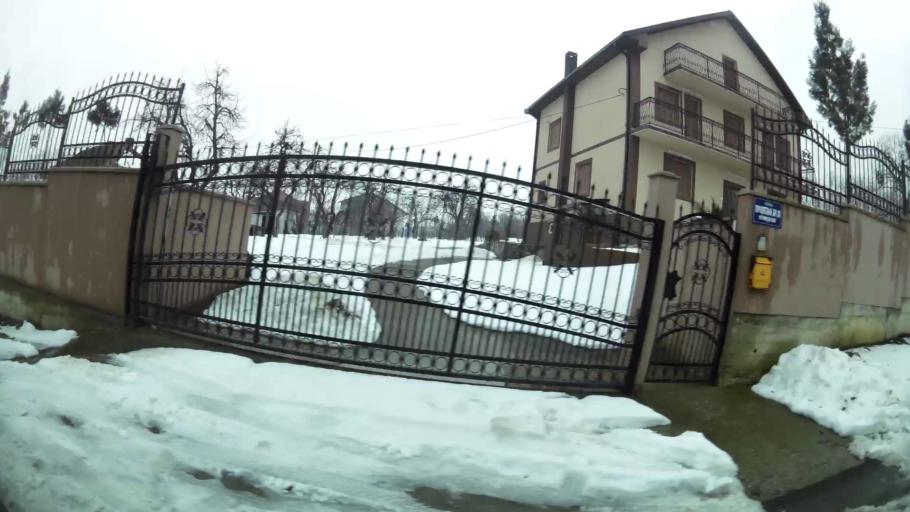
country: RS
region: Central Serbia
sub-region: Belgrade
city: Zvezdara
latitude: 44.7478
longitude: 20.5099
